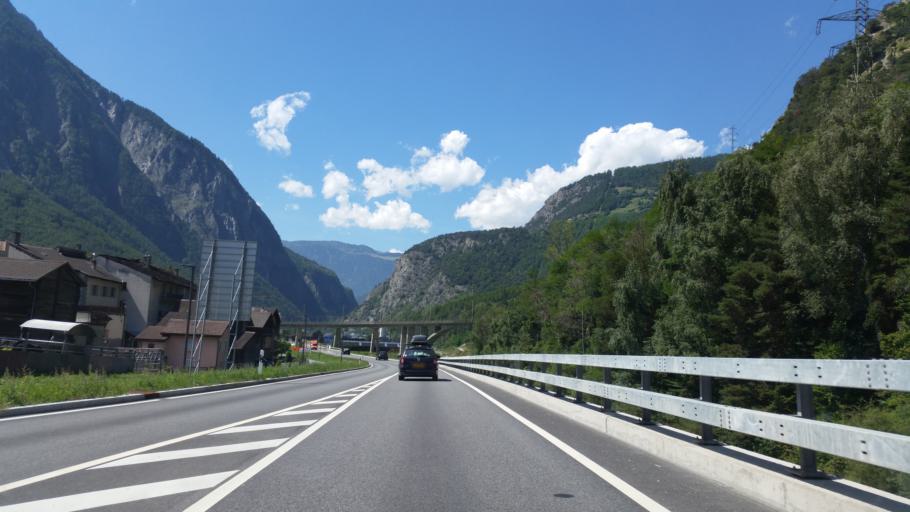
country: CH
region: Valais
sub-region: Martigny District
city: Charrat-les-Chenes
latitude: 46.0792
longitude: 7.1512
